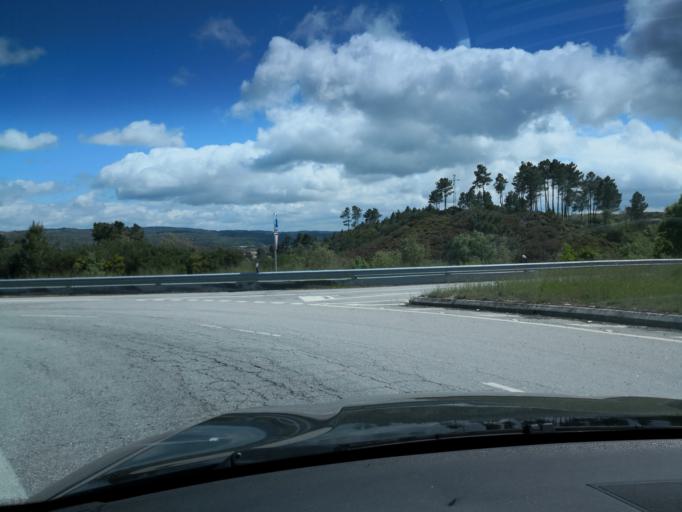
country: PT
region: Vila Real
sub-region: Vila Real
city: Vila Real
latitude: 41.3774
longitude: -7.7172
